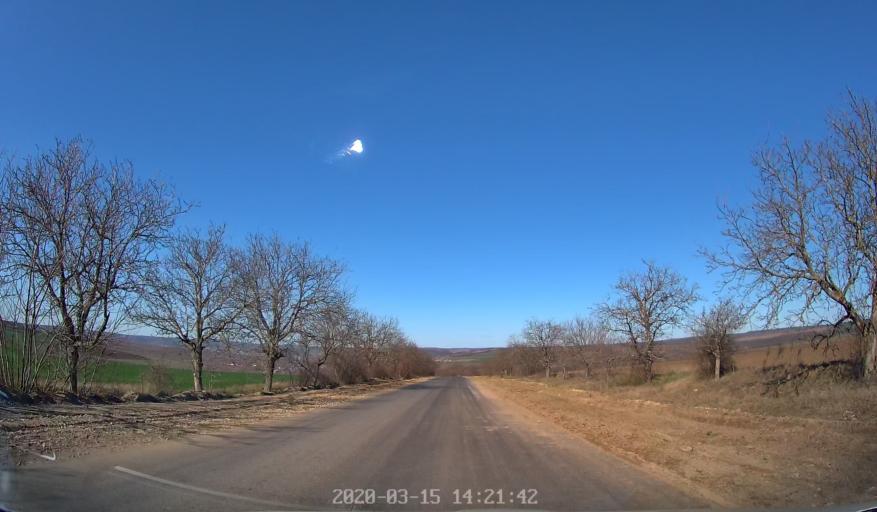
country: MD
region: Orhei
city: Orhei
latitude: 47.3209
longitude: 28.9255
